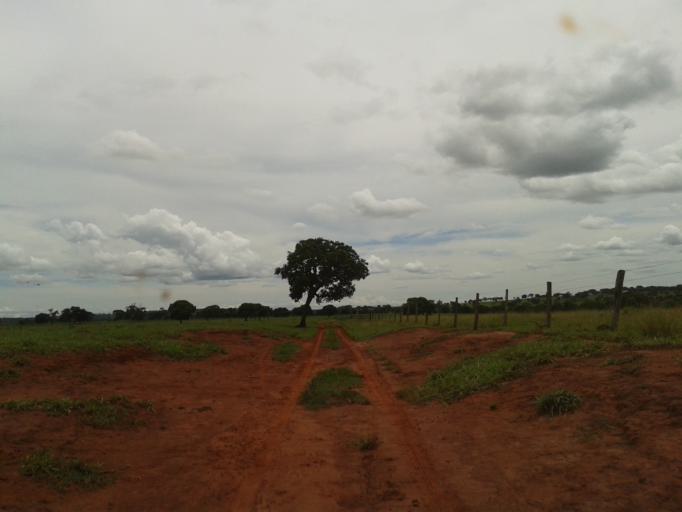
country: BR
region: Minas Gerais
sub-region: Santa Vitoria
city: Santa Vitoria
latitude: -18.7876
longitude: -49.8536
